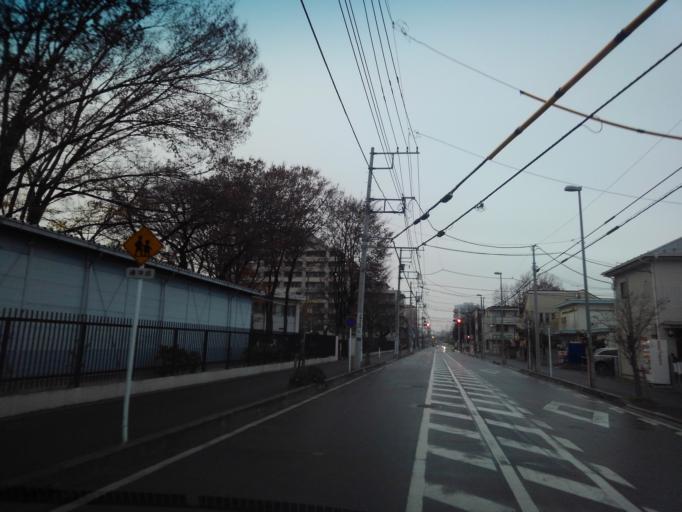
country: JP
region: Tokyo
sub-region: Machida-shi
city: Machida
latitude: 35.5203
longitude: 139.4428
